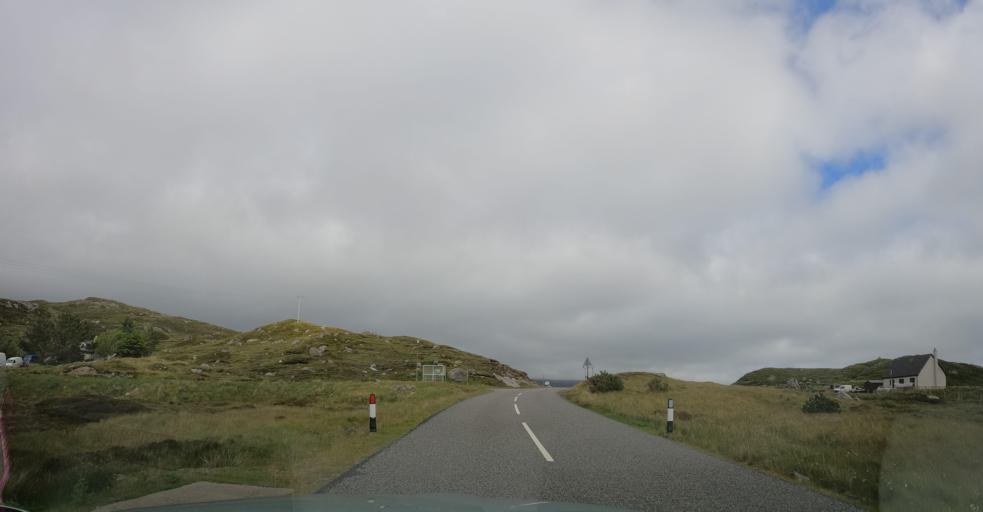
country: GB
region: Scotland
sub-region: Eilean Siar
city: Harris
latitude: 57.8888
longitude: -6.8071
